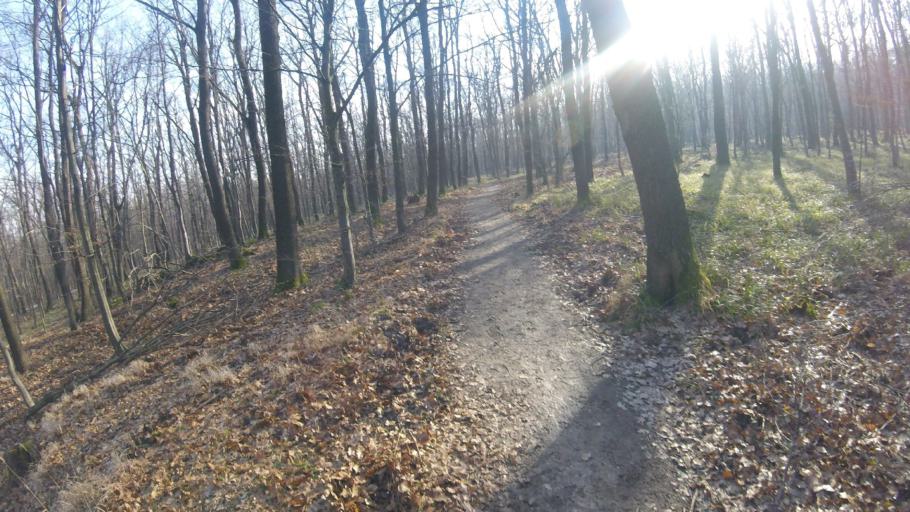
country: HU
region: Pest
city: Pilisszentkereszt
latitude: 47.6726
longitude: 18.9082
